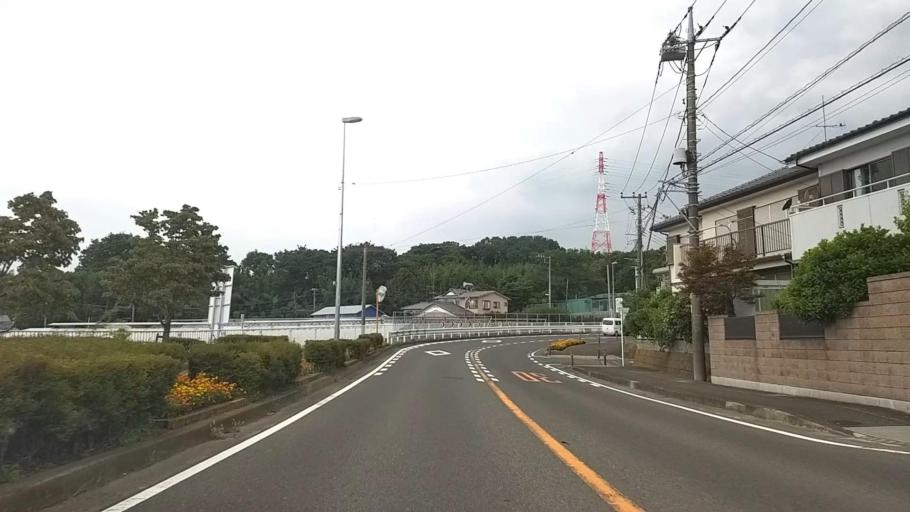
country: JP
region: Kanagawa
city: Isehara
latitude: 35.3897
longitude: 139.3257
